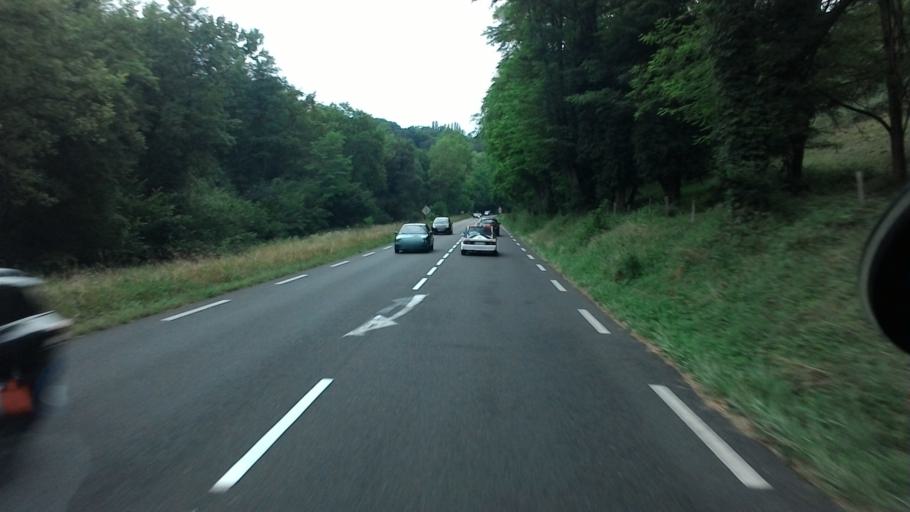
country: FR
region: Rhone-Alpes
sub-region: Departement de la Savoie
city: Yenne
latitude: 45.6967
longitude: 5.7985
